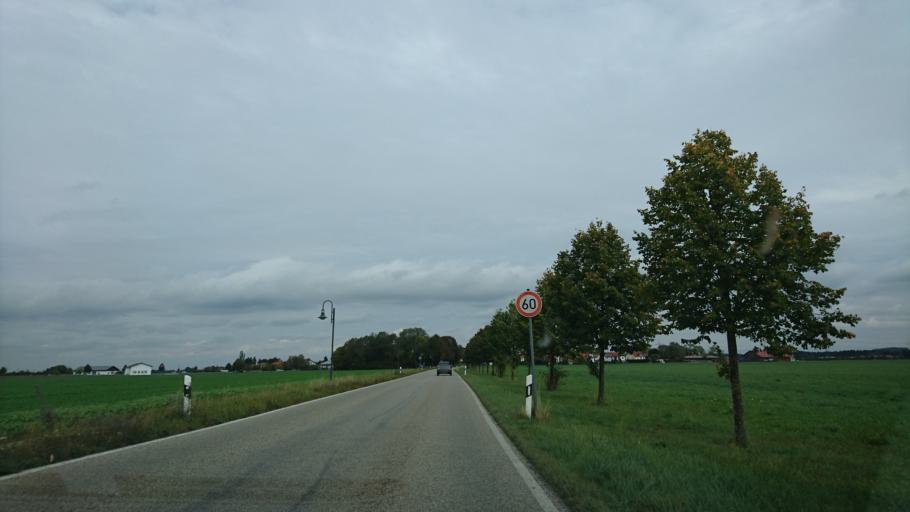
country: DE
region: Bavaria
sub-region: Upper Bavaria
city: Vaterstetten
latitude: 48.1092
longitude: 11.7935
